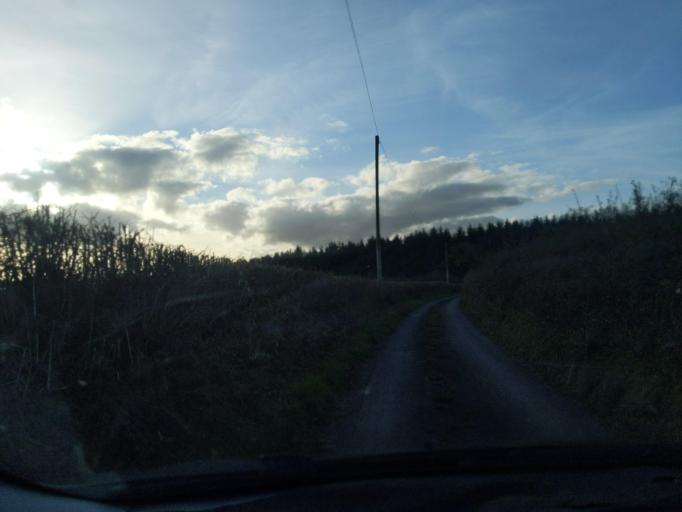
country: GB
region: England
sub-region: Devon
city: Bovey Tracey
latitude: 50.6311
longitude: -3.6753
